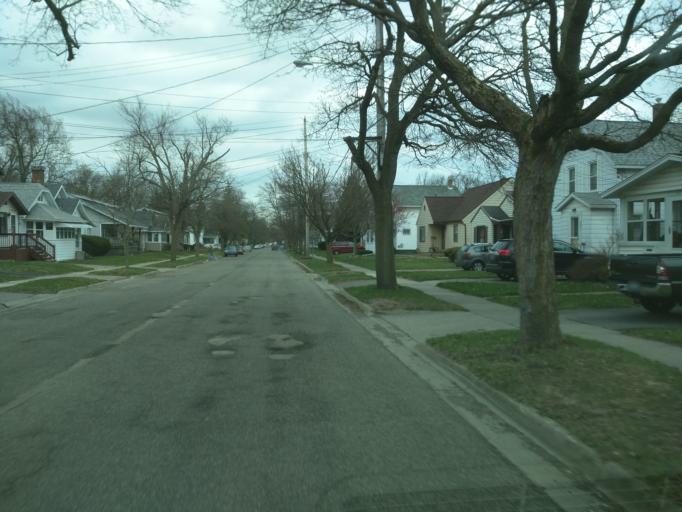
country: US
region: Michigan
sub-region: Ingham County
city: Lansing
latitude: 42.7399
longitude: -84.5224
